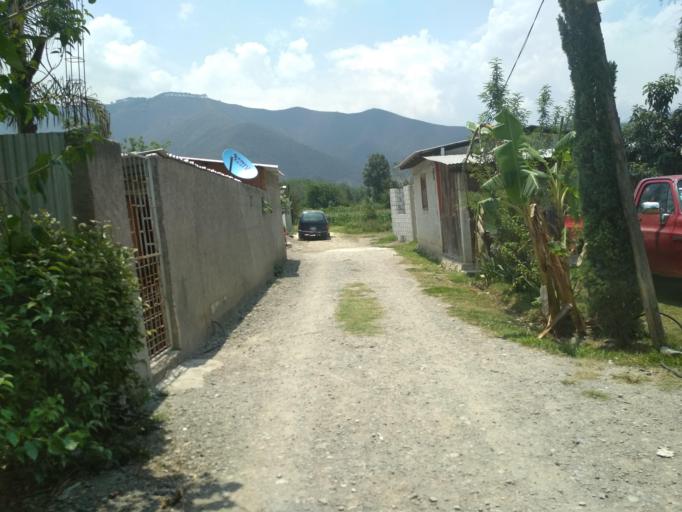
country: MX
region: Veracruz
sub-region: Acultzingo
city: Acatla
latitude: 18.7665
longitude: -97.2166
